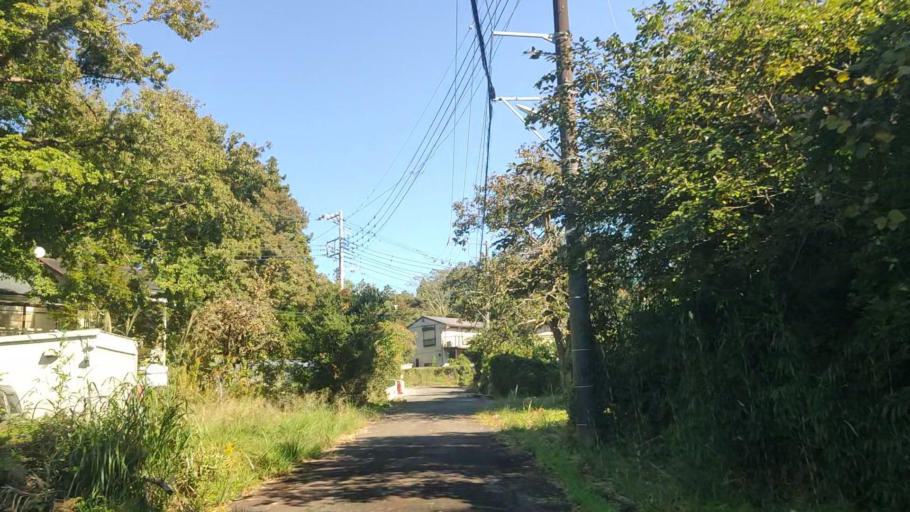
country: JP
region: Shizuoka
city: Ito
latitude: 34.9460
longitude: 139.0112
